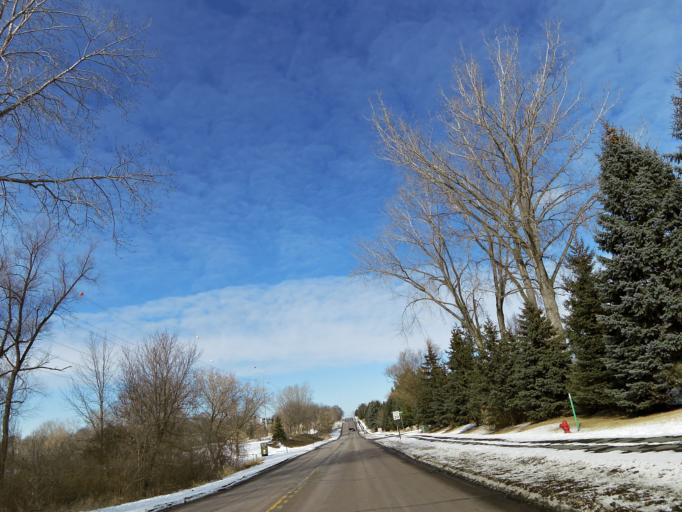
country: US
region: Minnesota
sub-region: Hennepin County
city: Eden Prairie
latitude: 44.8225
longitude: -93.4291
